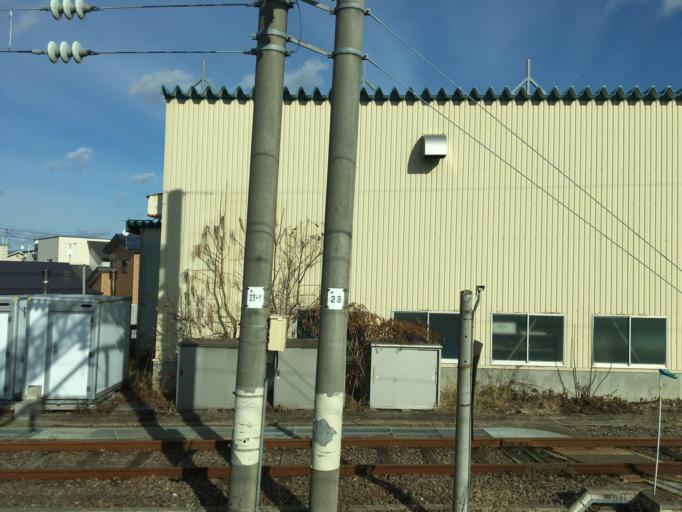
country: JP
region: Akita
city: Omagari
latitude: 39.4676
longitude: 140.4776
